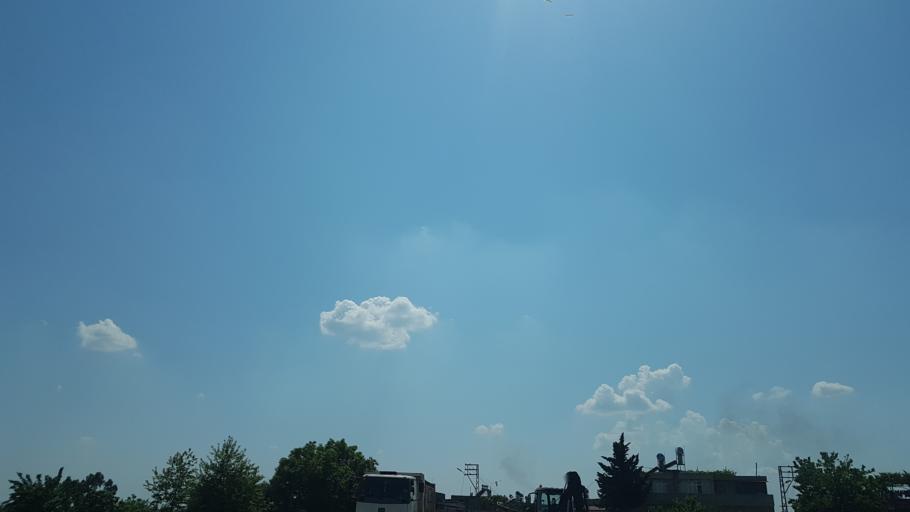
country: TR
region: Adana
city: Yuregir
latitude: 37.0106
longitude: 35.3892
